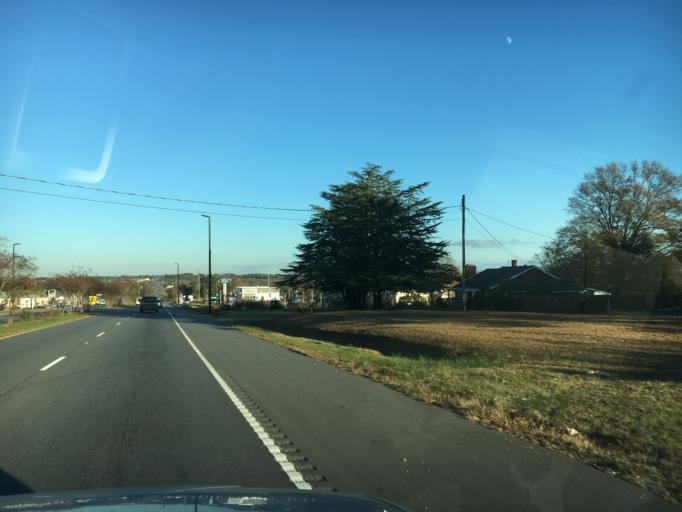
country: US
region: South Carolina
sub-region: Greenville County
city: Greer
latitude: 34.9487
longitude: -82.1985
